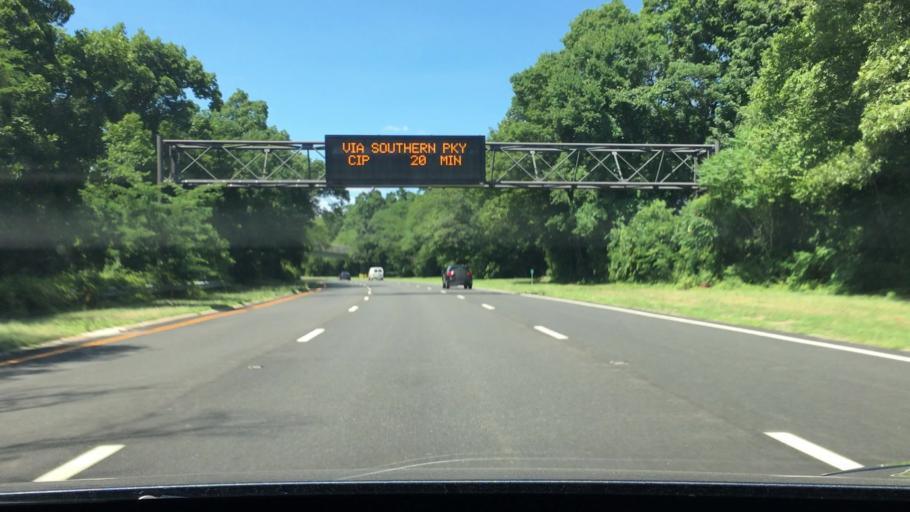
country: US
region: New York
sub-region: Nassau County
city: Wantagh
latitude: 40.6864
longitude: -73.5139
